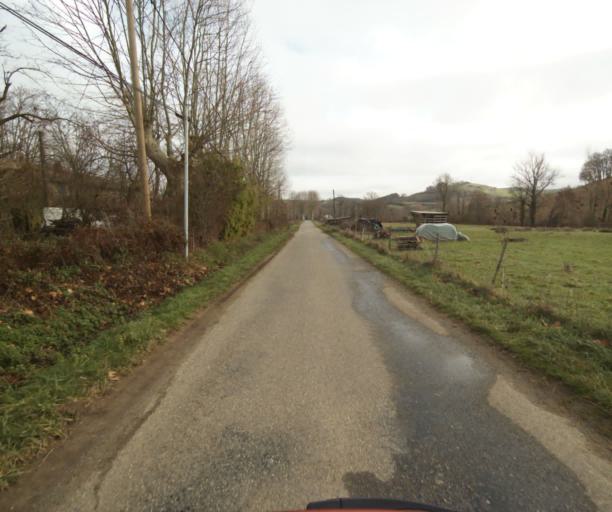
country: FR
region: Midi-Pyrenees
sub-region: Departement de la Haute-Garonne
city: Gaillac-Toulza
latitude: 43.1658
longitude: 1.4890
